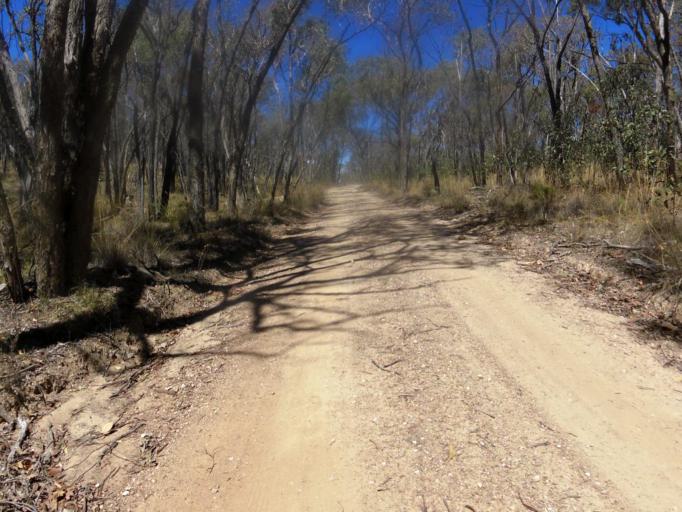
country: AU
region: Victoria
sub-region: Mount Alexander
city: Castlemaine
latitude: -37.0014
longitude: 144.1092
